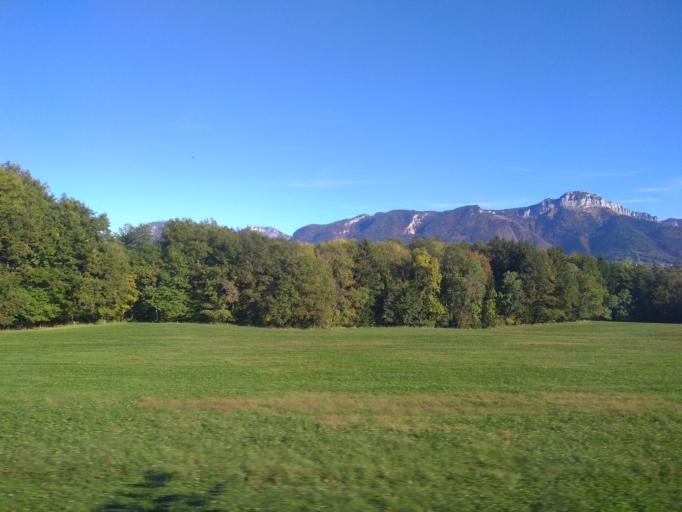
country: FR
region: Rhone-Alpes
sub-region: Departement de la Haute-Savoie
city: Saint-Martin-Bellevue
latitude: 45.9888
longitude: 6.1568
